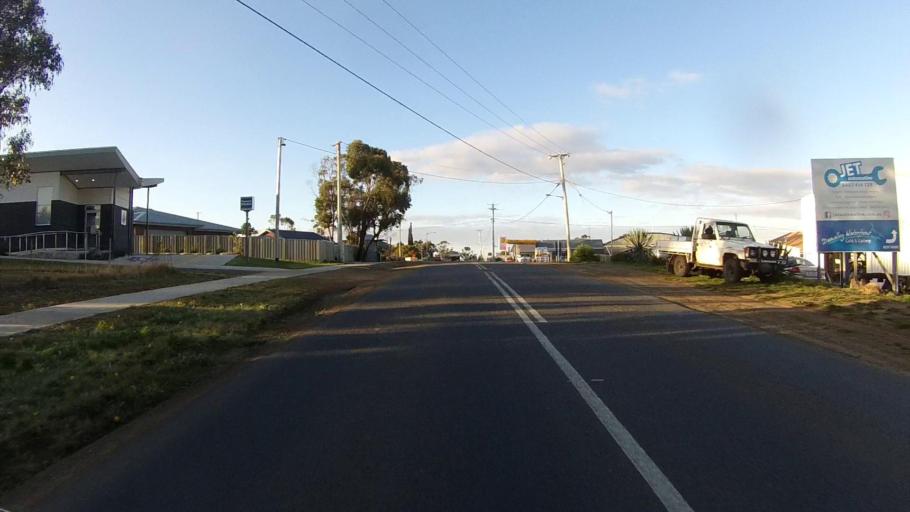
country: AU
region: Tasmania
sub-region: Sorell
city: Sorell
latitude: -42.8877
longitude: 147.8104
